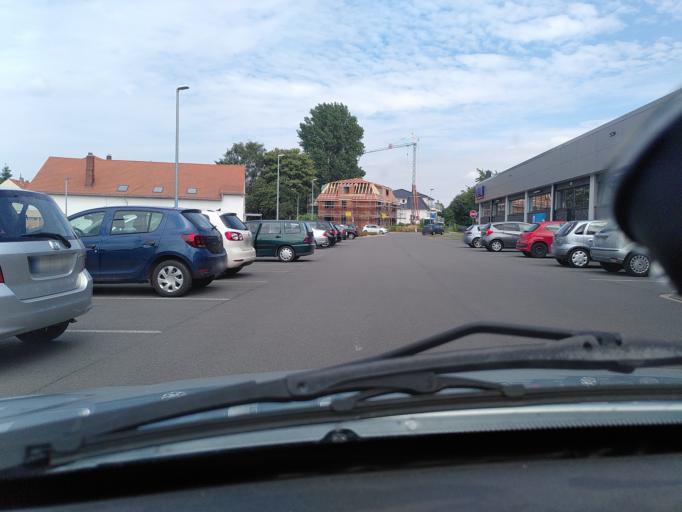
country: DE
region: North Rhine-Westphalia
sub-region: Regierungsbezirk Detmold
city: Minden
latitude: 52.2728
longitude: 8.8871
